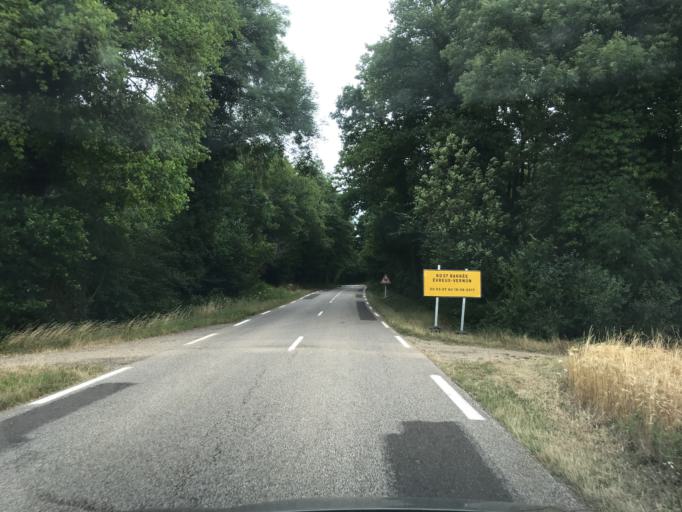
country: FR
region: Haute-Normandie
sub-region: Departement de l'Eure
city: Menilles
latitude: 49.0394
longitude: 1.3021
